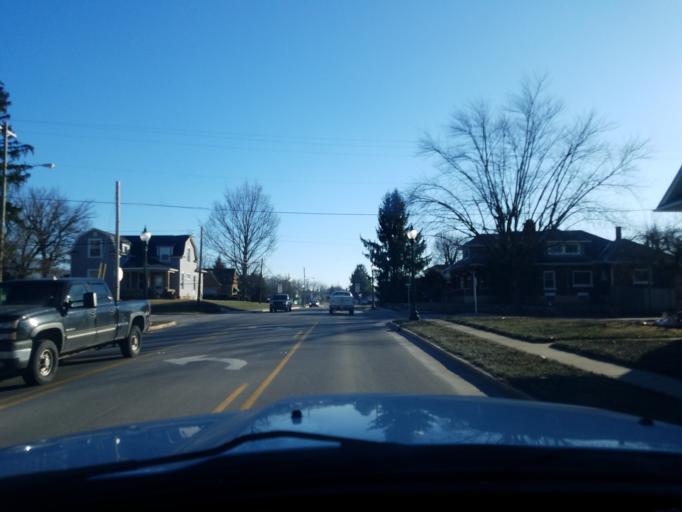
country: US
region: Indiana
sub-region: Orange County
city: Orleans
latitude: 38.6587
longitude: -86.4528
